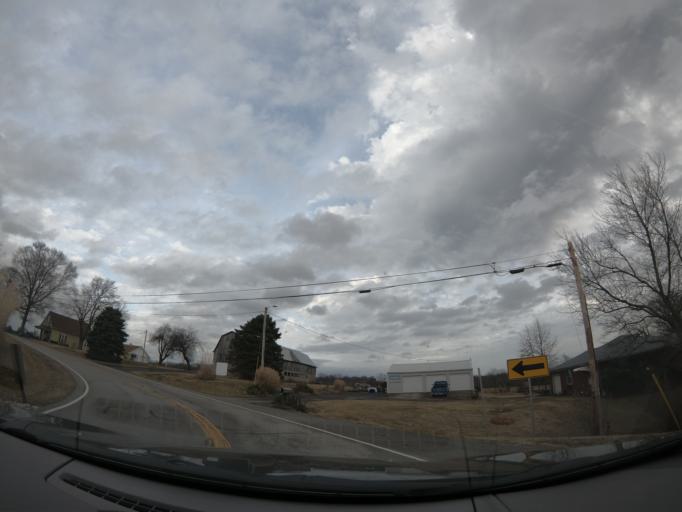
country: US
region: Indiana
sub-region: Floyd County
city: Galena
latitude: 38.4013
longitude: -85.9091
